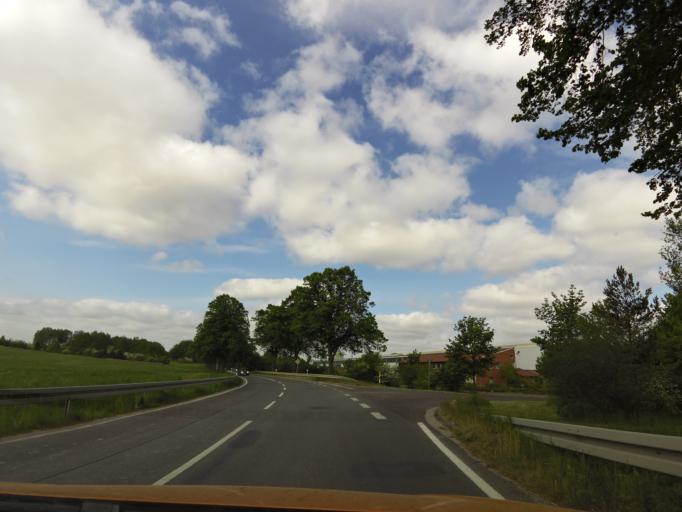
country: DE
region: Brandenburg
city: Gorzke
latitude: 52.1094
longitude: 12.3896
